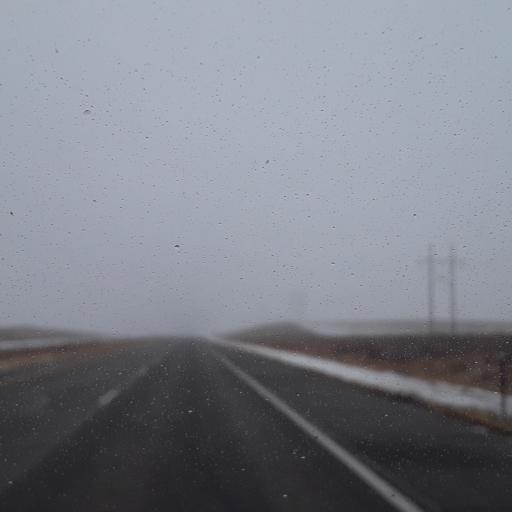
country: US
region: Colorado
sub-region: Logan County
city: Sterling
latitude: 40.7837
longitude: -102.9070
